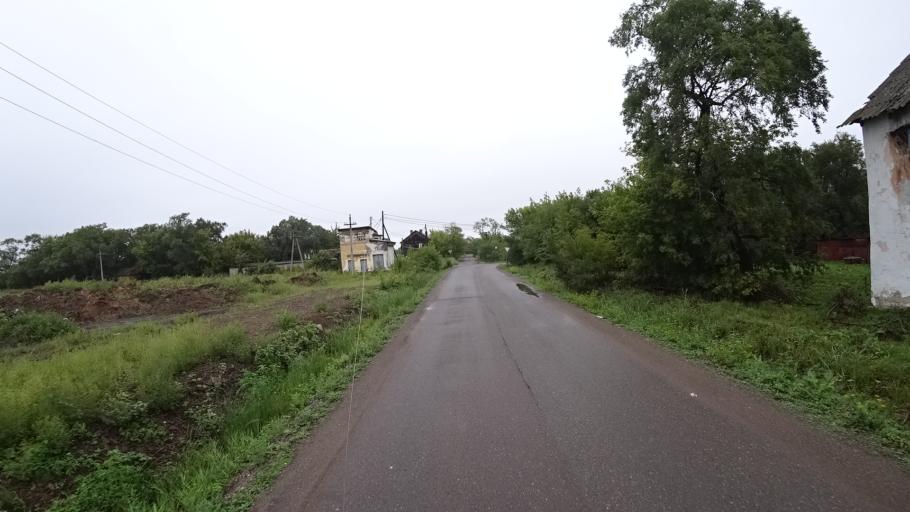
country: RU
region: Primorskiy
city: Monastyrishche
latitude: 44.1981
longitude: 132.4257
